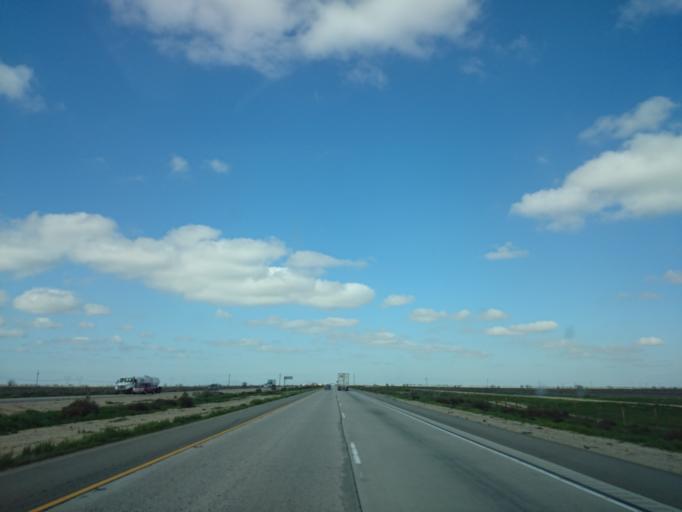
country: US
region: California
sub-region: Kern County
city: Rosedale
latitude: 35.3174
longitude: -119.2829
